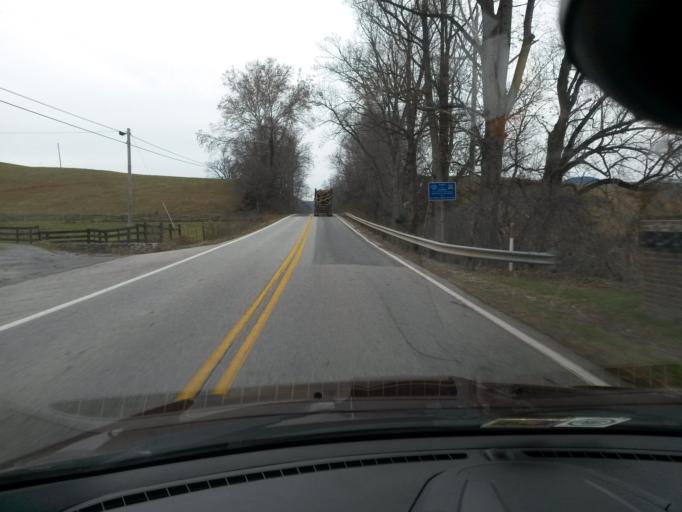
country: US
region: Virginia
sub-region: Amherst County
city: Amherst
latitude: 37.6511
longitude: -79.1340
